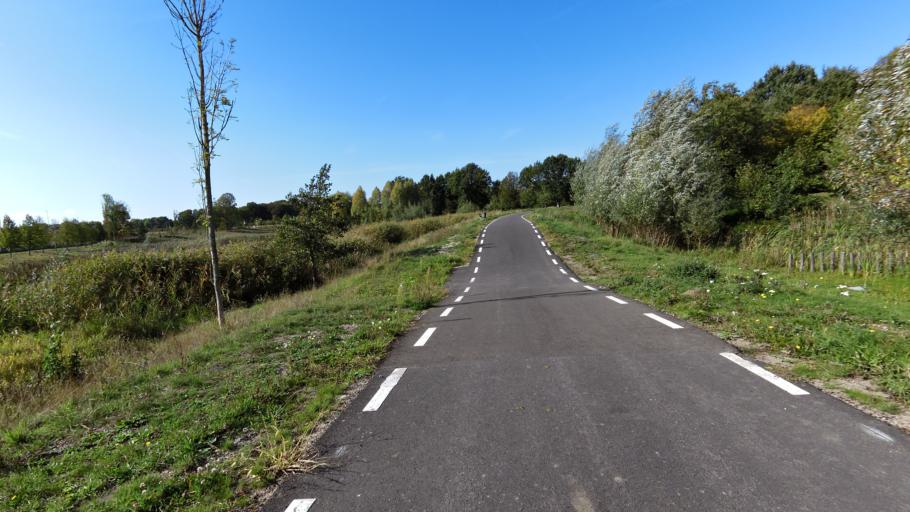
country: NL
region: Limburg
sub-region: Gemeente Onderbanken
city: Schinveld
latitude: 50.9608
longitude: 5.9785
